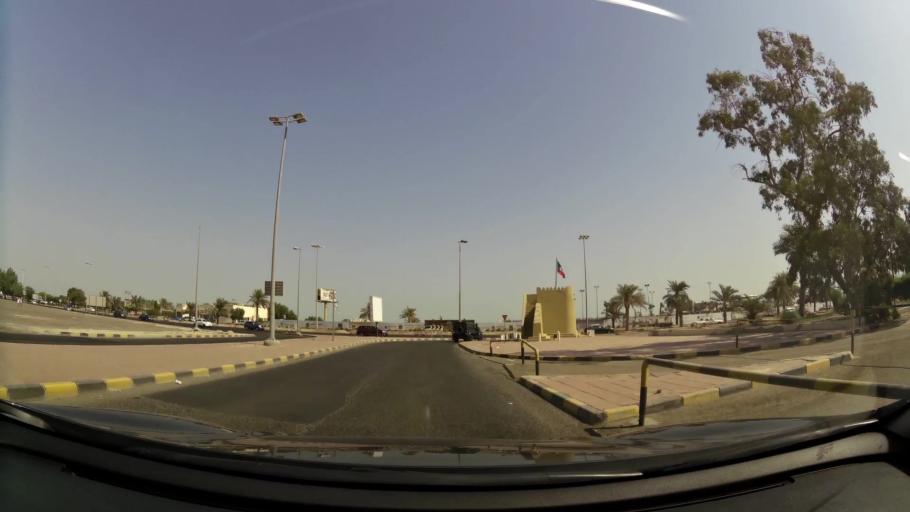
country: KW
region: Al Asimah
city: Ad Dasmah
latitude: 29.3789
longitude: 48.0025
